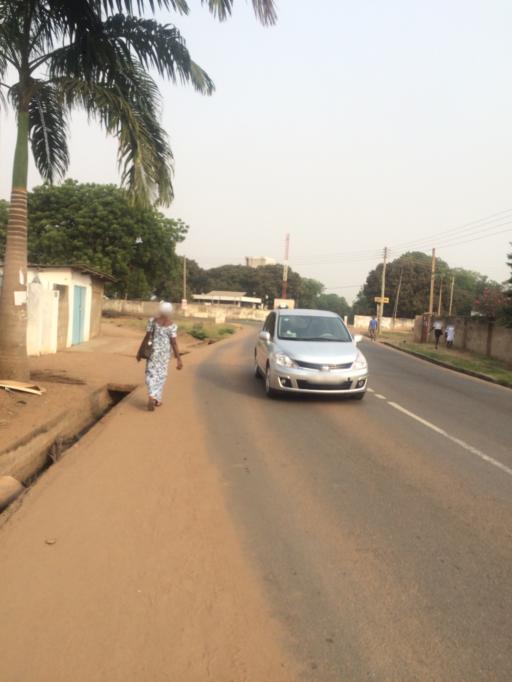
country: GH
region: Greater Accra
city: Nungua
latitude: 5.6047
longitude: -0.0833
